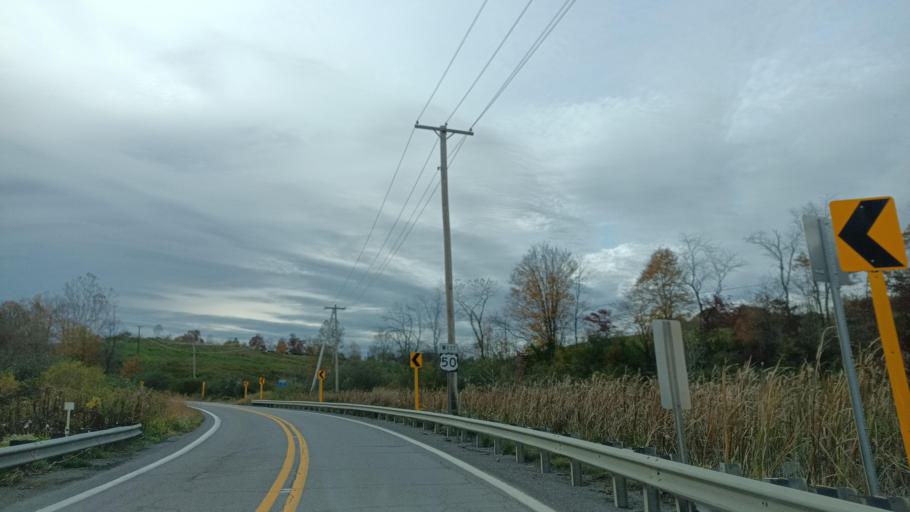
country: US
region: West Virginia
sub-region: Taylor County
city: Grafton
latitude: 39.3386
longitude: -79.8561
